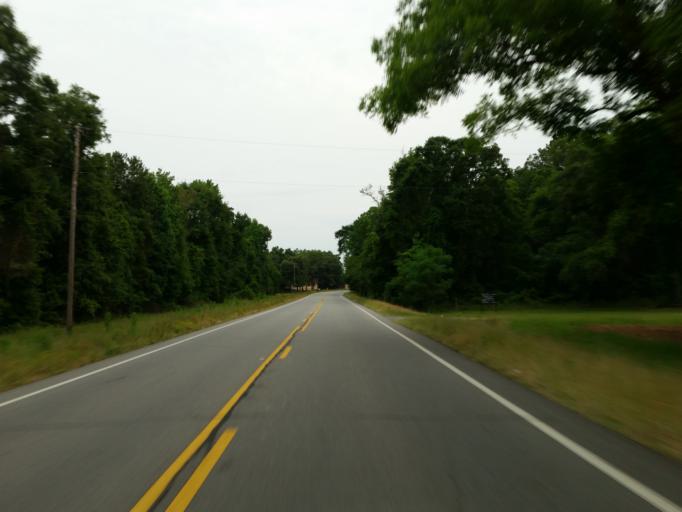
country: US
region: Georgia
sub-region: Dooly County
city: Unadilla
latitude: 32.2261
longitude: -83.7576
